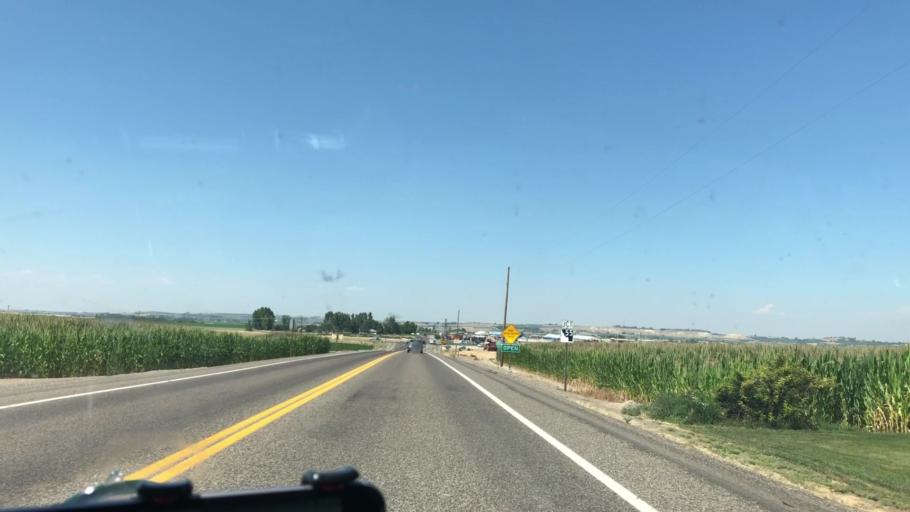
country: US
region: Idaho
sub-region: Owyhee County
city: Marsing
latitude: 43.5409
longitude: -116.8517
